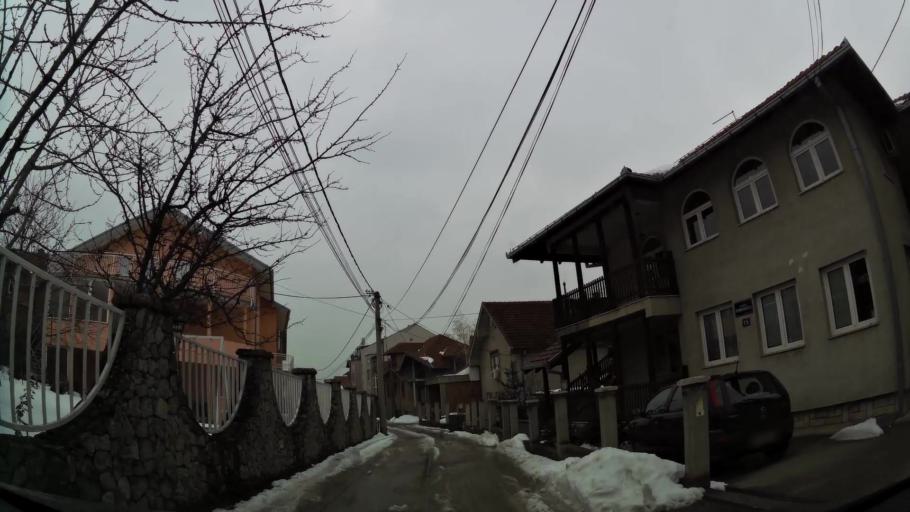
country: RS
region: Central Serbia
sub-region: Belgrade
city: Zvezdara
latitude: 44.7679
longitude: 20.5110
